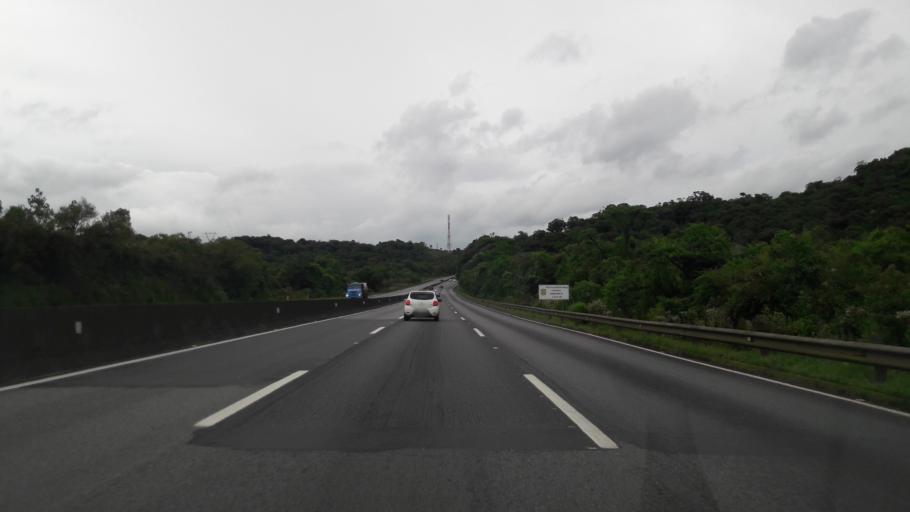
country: BR
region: Parana
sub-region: Piraquara
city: Piraquara
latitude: -25.5884
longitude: -48.9416
